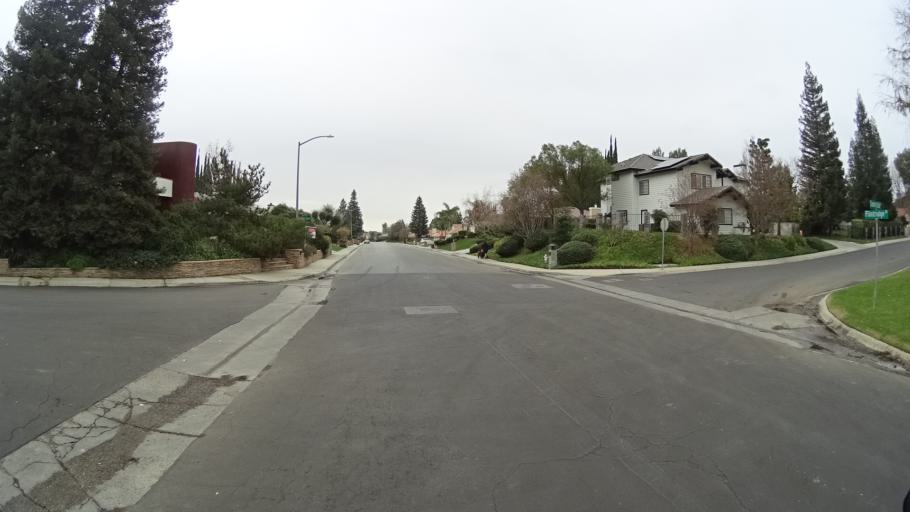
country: US
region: California
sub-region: Kern County
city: Bakersfield
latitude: 35.3871
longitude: -118.9336
